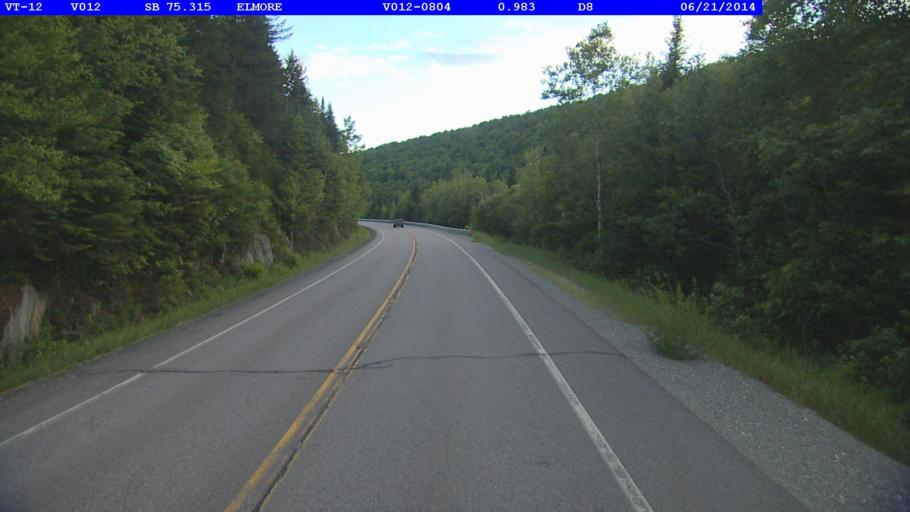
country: US
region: Vermont
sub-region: Lamoille County
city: Morrisville
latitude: 44.4654
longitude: -72.5424
